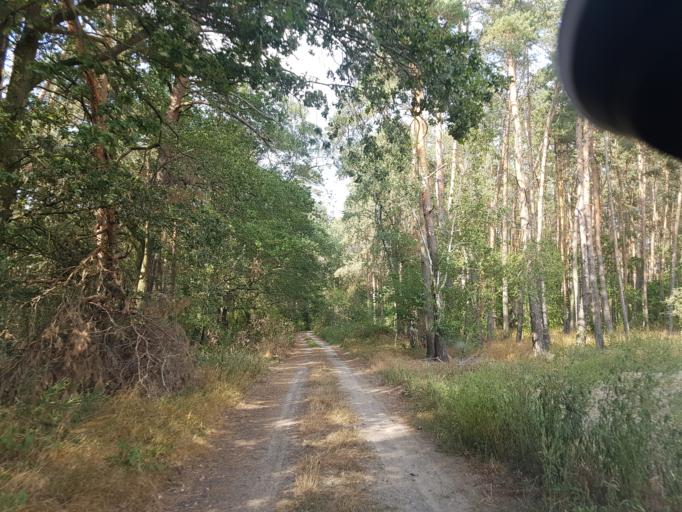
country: DE
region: Brandenburg
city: Calau
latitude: 51.7620
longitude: 13.9517
